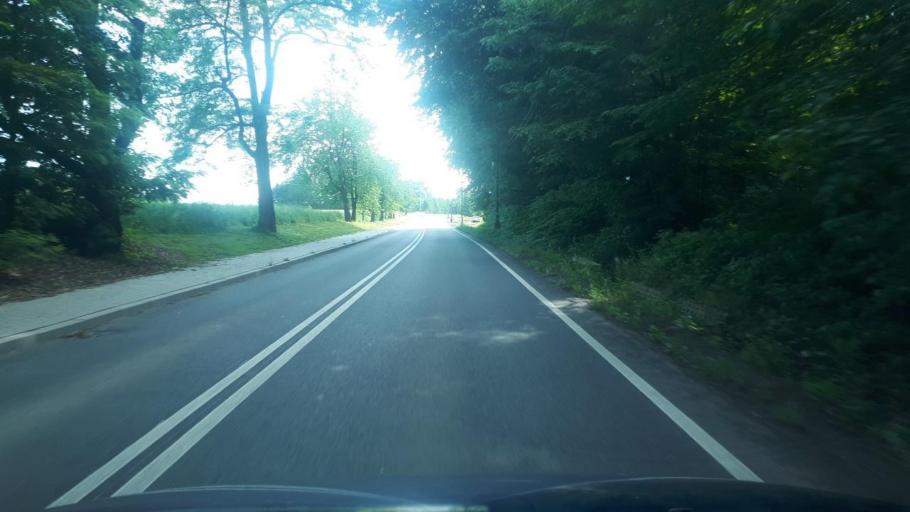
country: PL
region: Silesian Voivodeship
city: Janowice
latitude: 49.9059
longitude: 19.0847
